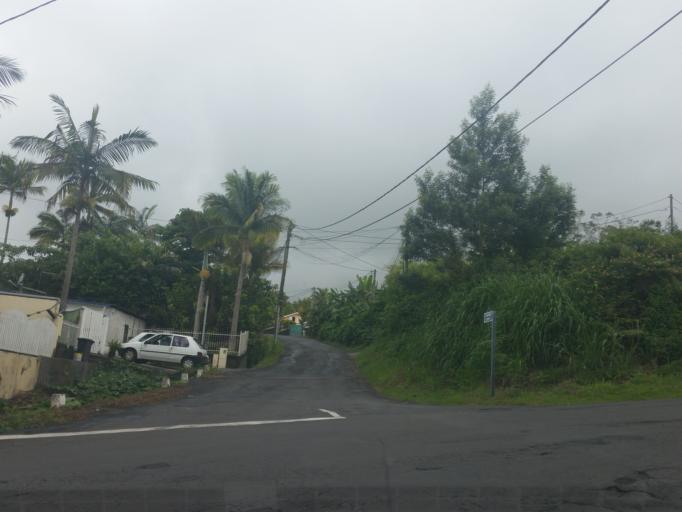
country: RE
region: Reunion
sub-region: Reunion
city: Le Tampon
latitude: -21.2381
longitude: 55.5190
